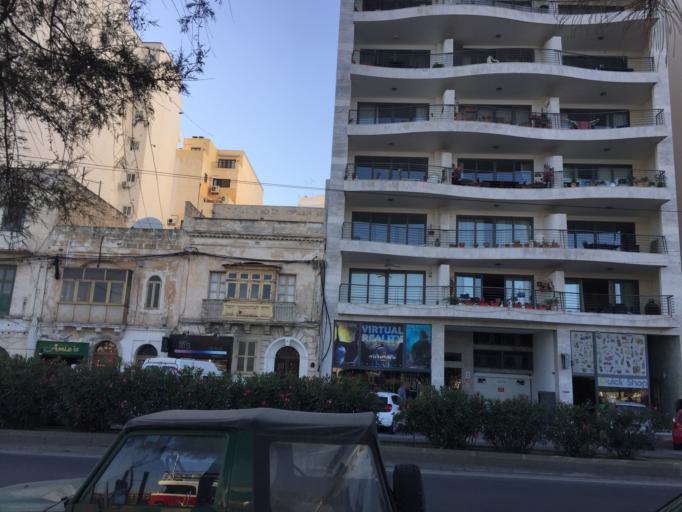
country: MT
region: Tas-Sliema
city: Sliema
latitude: 35.9081
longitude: 14.5015
